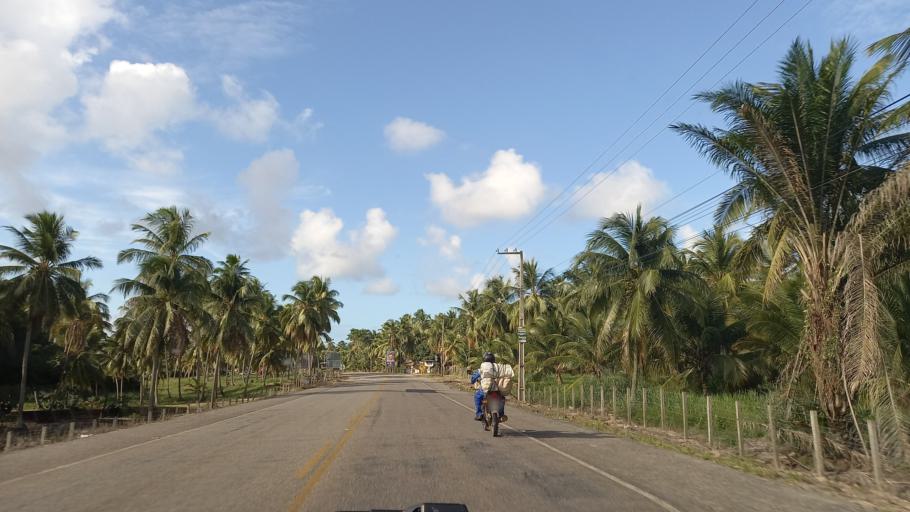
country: BR
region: Pernambuco
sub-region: Tamandare
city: Tamandare
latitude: -8.7084
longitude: -35.0882
